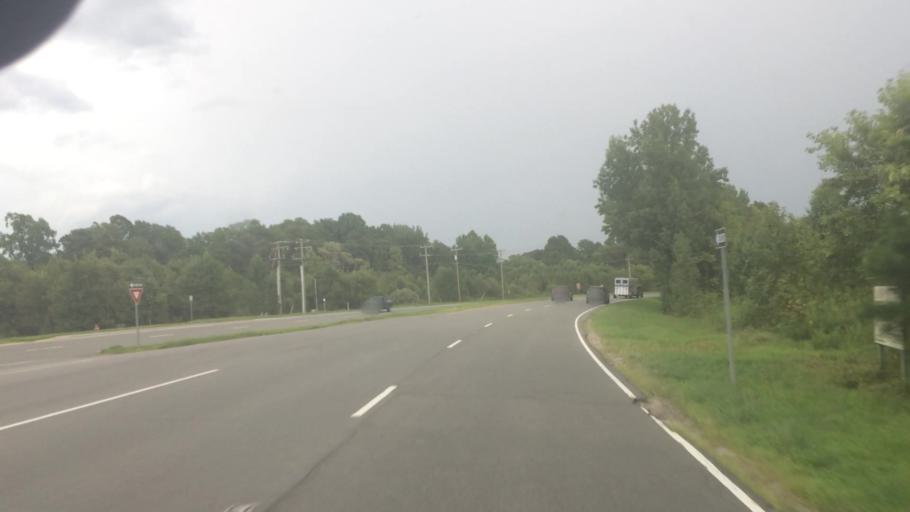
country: US
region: Virginia
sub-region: King William County
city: West Point
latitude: 37.4093
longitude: -76.8112
